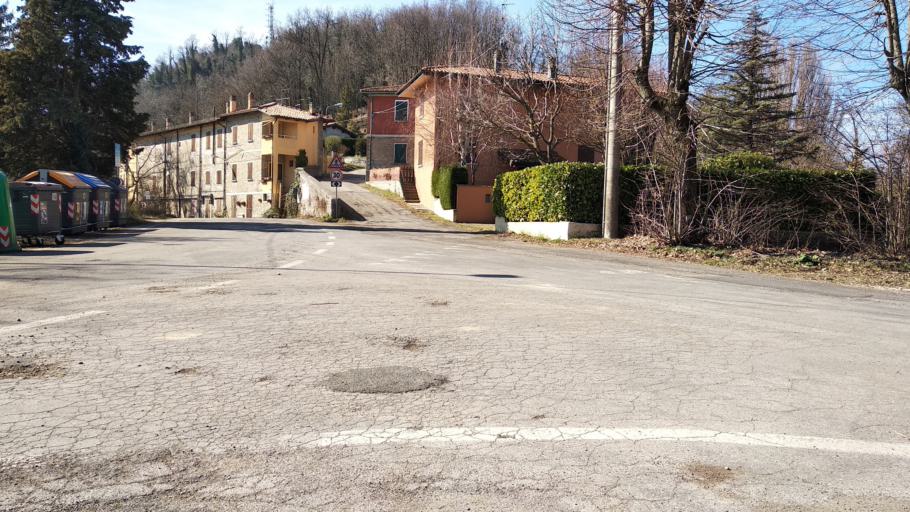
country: IT
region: Emilia-Romagna
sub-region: Provincia di Bologna
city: Osteria Grande
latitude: 44.3621
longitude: 11.4892
